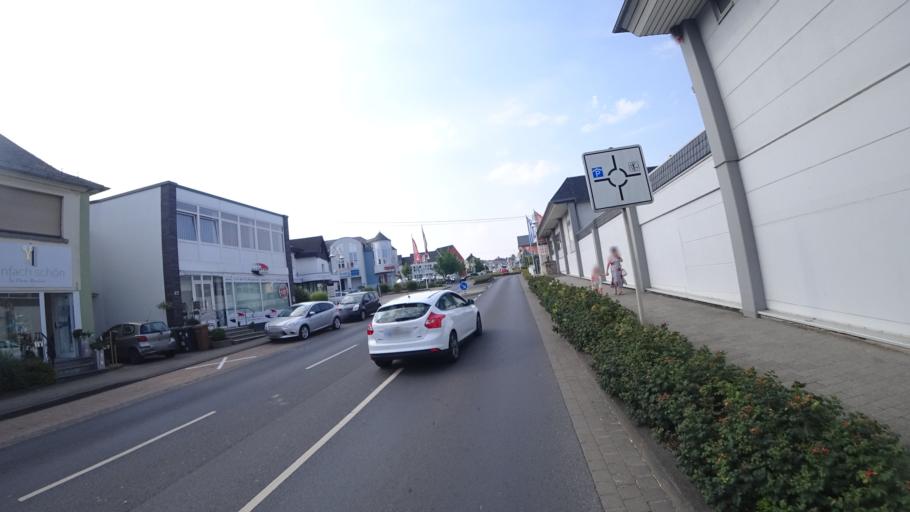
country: DE
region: Rheinland-Pfalz
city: Ransbach-Baumbach
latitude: 50.4661
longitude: 7.7265
